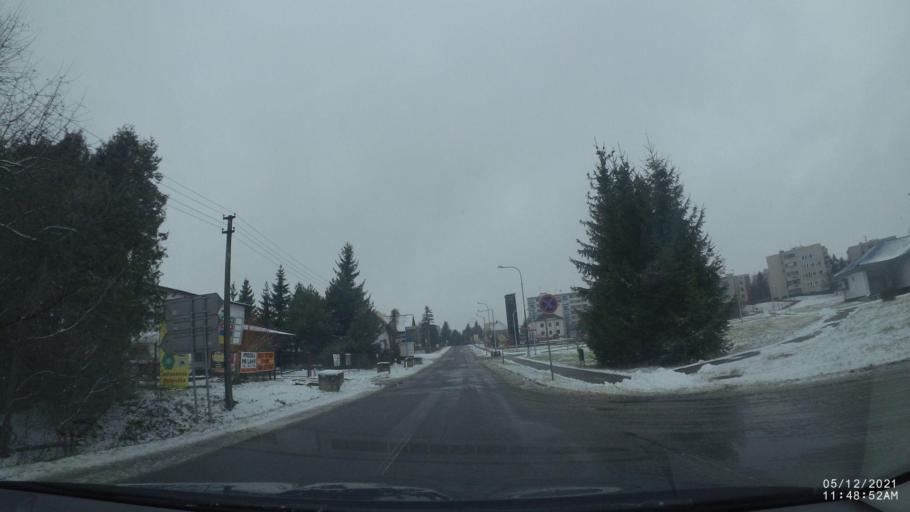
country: CZ
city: Dobruska
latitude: 50.2882
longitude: 16.1672
